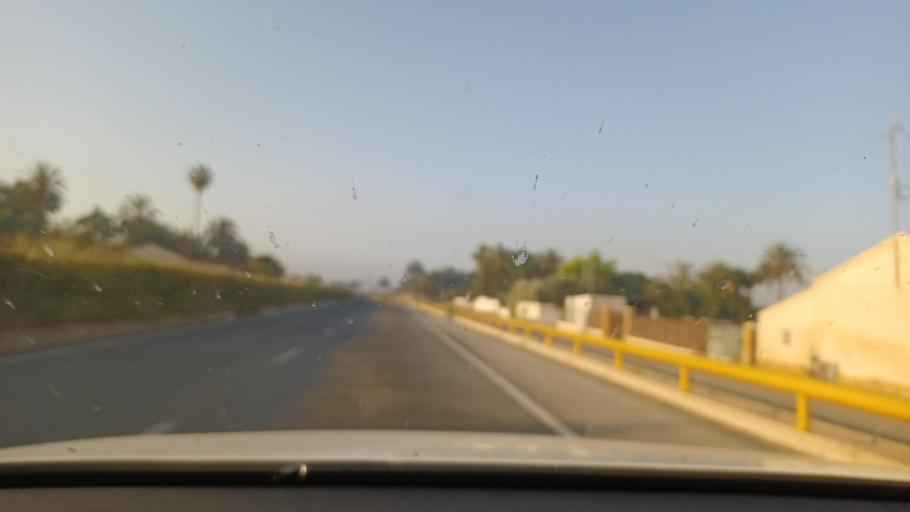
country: ES
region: Valencia
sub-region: Provincia de Alicante
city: Elche
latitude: 38.2004
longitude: -0.7005
